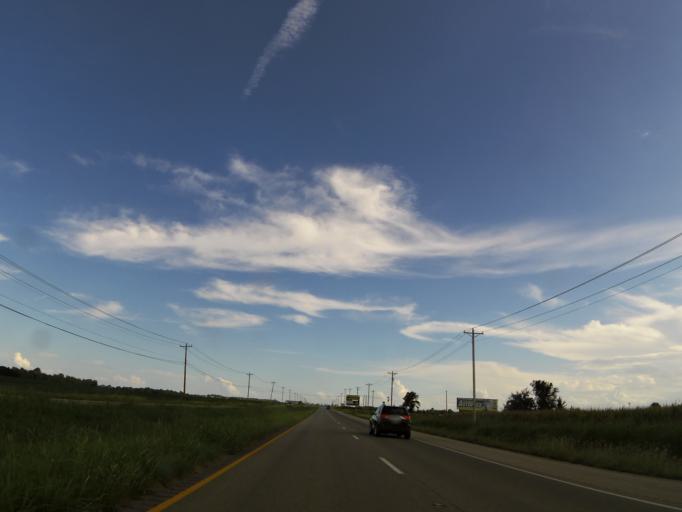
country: US
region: Kentucky
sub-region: Christian County
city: Oak Grove
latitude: 36.7175
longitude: -87.4594
